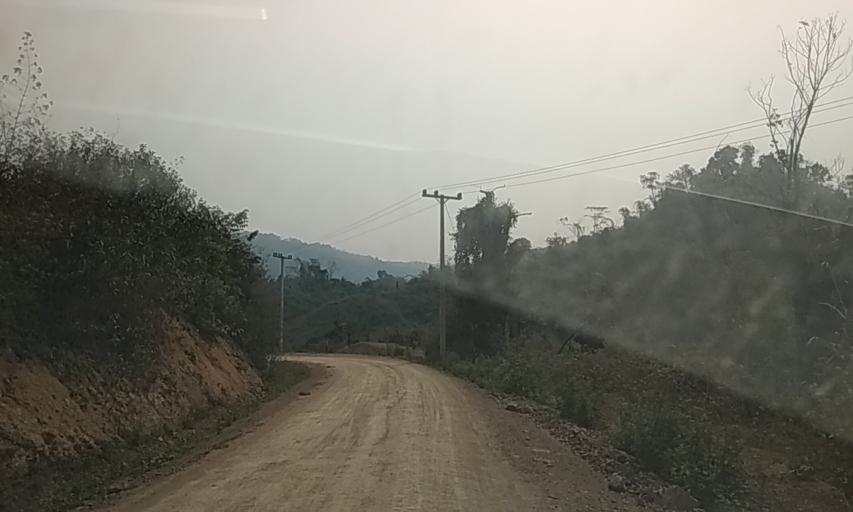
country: VN
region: Huyen Dien Bien
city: Dien Bien Phu
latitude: 21.4216
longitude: 102.7591
